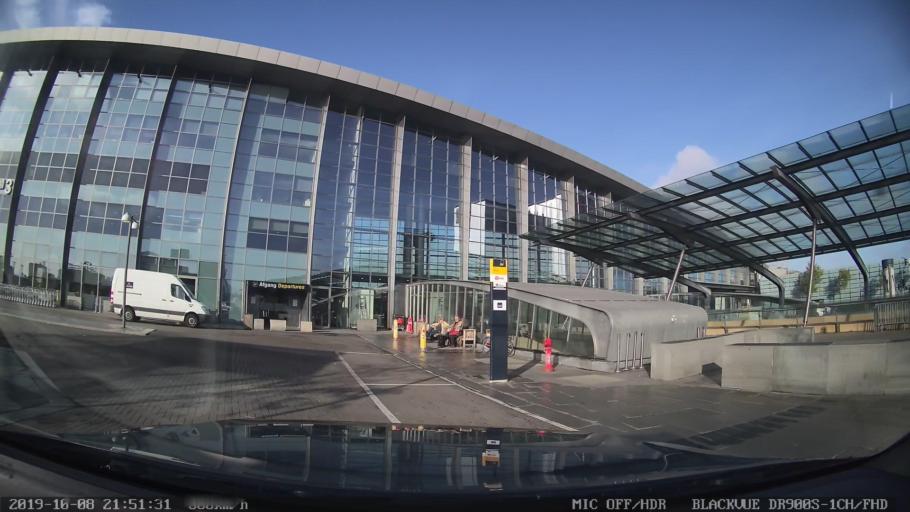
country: DK
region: Capital Region
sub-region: Dragor Kommune
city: Dragor
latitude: 55.6291
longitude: 12.6538
